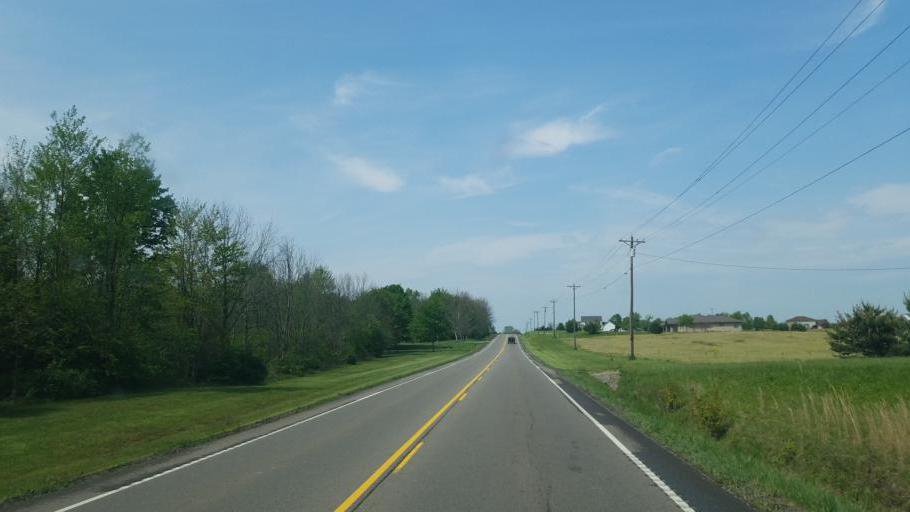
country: US
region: Ohio
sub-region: Licking County
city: Hebron
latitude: 39.9979
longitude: -82.5245
